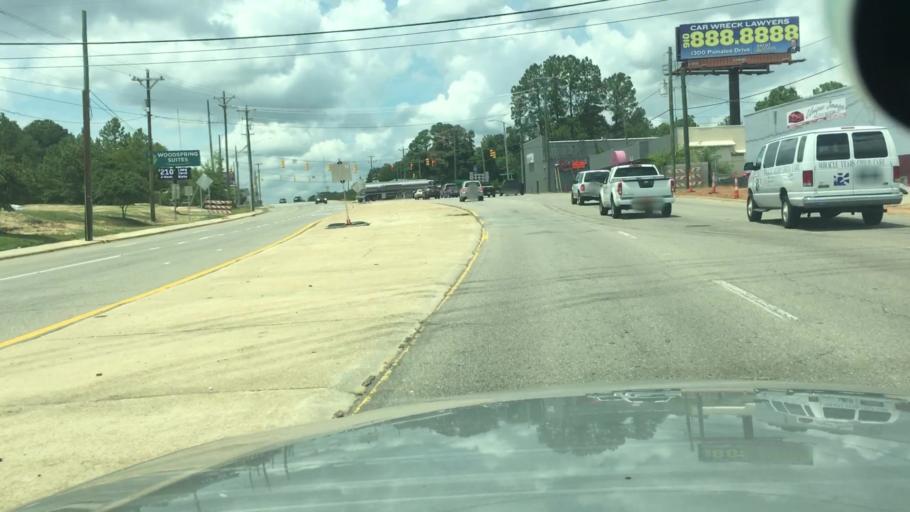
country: US
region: North Carolina
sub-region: Cumberland County
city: Fayetteville
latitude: 35.0614
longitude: -78.8889
